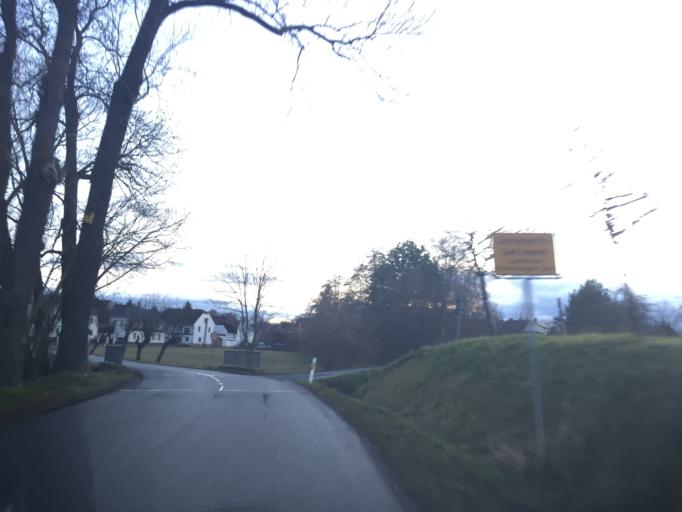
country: DE
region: Thuringia
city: Schmolln
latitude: 50.8809
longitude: 12.3327
